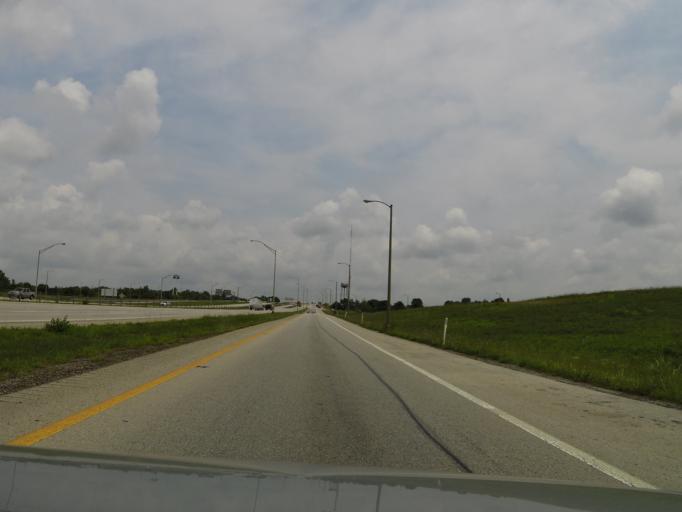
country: US
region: Kentucky
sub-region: Hardin County
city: Elizabethtown
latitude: 37.6742
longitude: -85.8499
